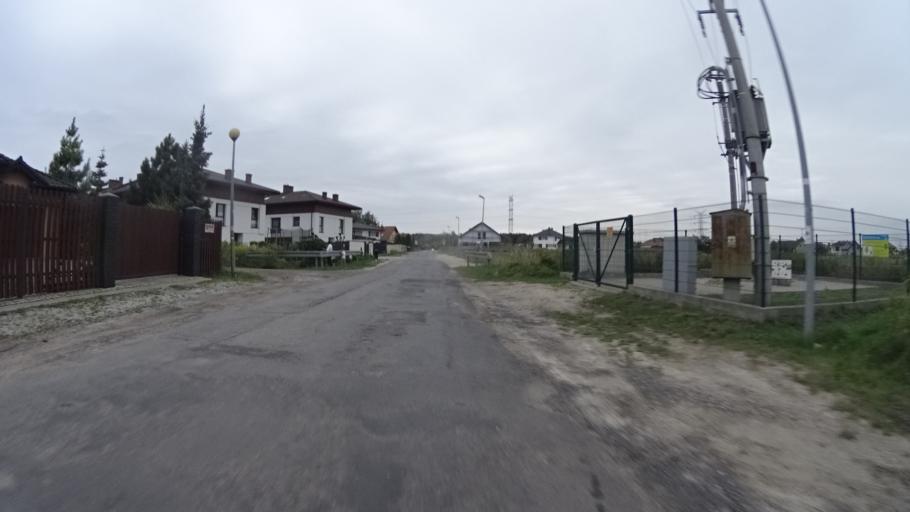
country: PL
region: Masovian Voivodeship
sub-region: Powiat warszawski zachodni
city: Stare Babice
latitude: 52.2576
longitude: 20.8207
